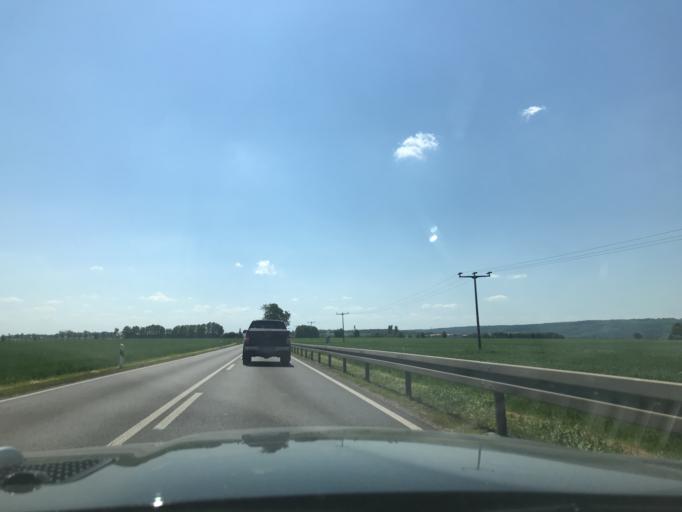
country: DE
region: Thuringia
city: Westhausen
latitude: 51.0095
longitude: 10.6851
